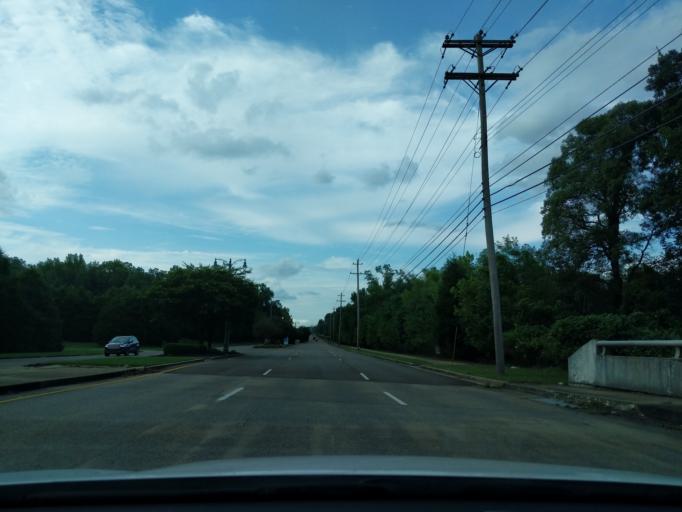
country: US
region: Tennessee
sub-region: Shelby County
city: Germantown
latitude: 35.0335
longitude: -89.7597
